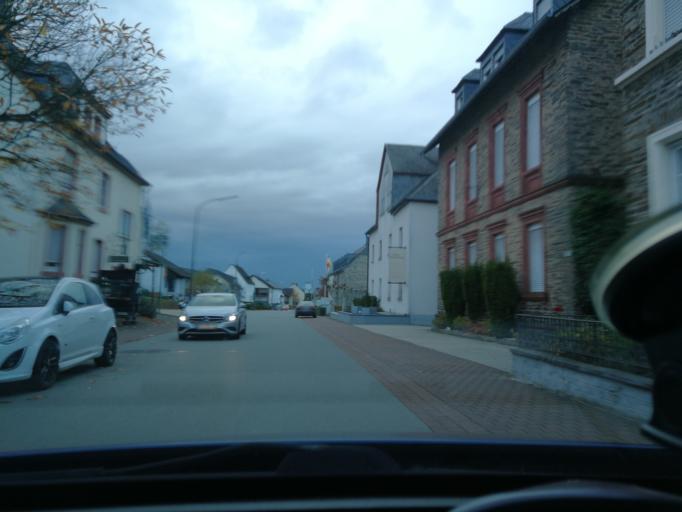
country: DE
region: Rheinland-Pfalz
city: Osann-Monzel
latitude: 49.9113
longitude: 6.9547
